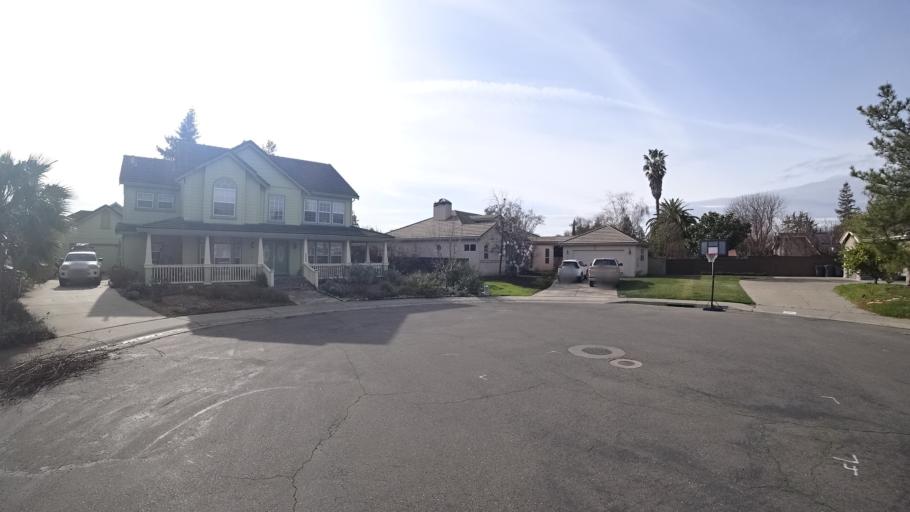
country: US
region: California
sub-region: Yolo County
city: Davis
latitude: 38.5504
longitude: -121.6827
